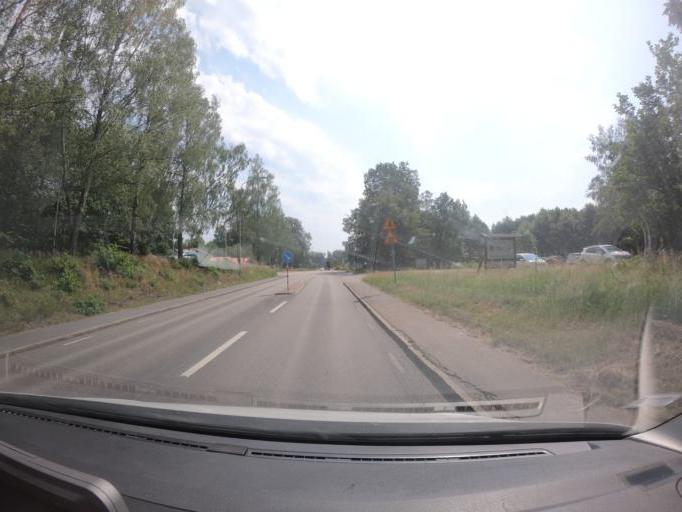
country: SE
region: Skane
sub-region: Hassleholms Kommun
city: Bjarnum
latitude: 56.3521
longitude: 13.6621
